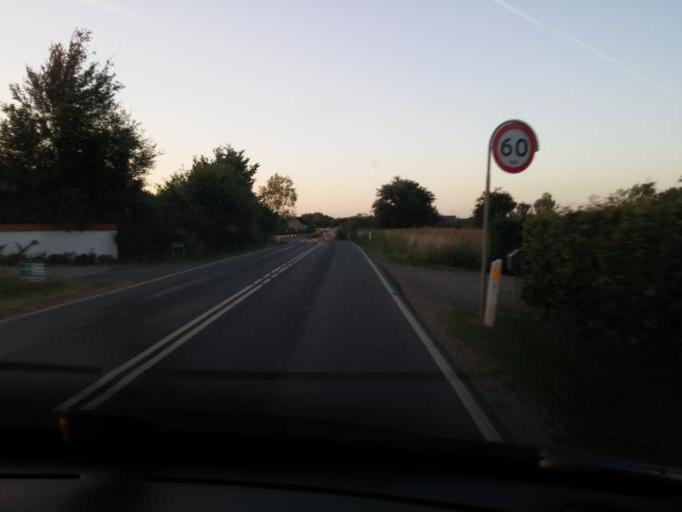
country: DK
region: South Denmark
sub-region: Langeland Kommune
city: Rudkobing
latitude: 54.8894
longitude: 10.7335
